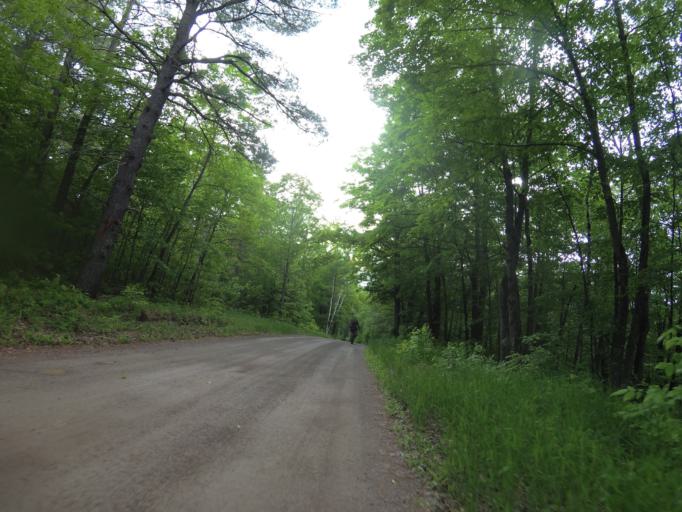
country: CA
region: Ontario
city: Renfrew
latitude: 45.1854
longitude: -76.9098
